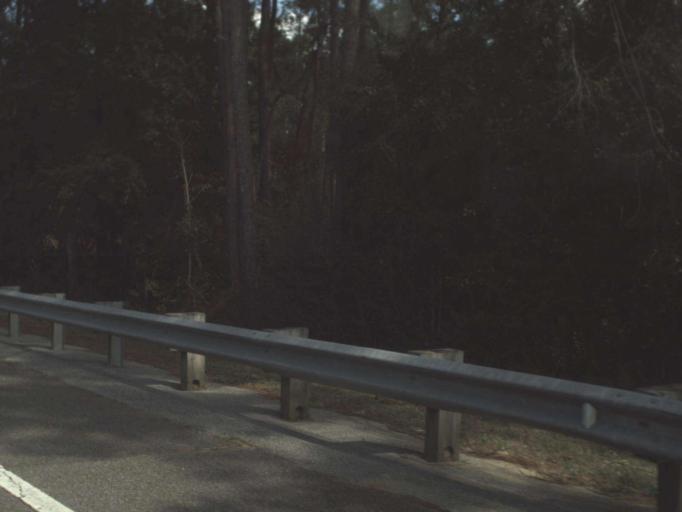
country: US
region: Florida
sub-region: Walton County
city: DeFuniak Springs
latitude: 30.9018
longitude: -86.1306
